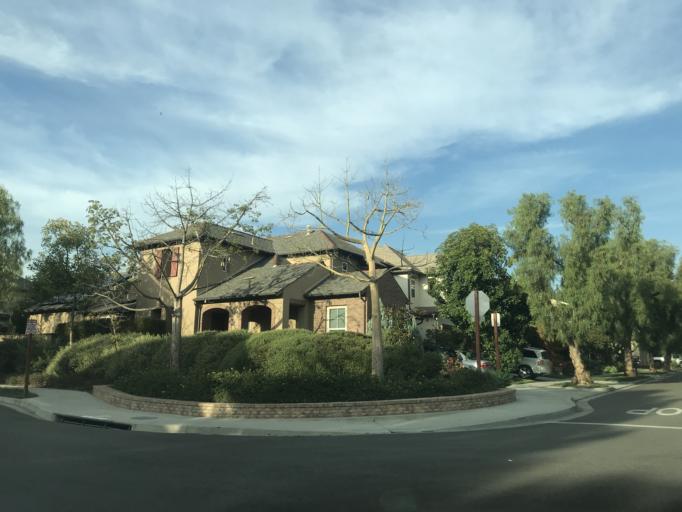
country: US
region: California
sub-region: Orange County
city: North Tustin
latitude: 33.7047
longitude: -117.7492
